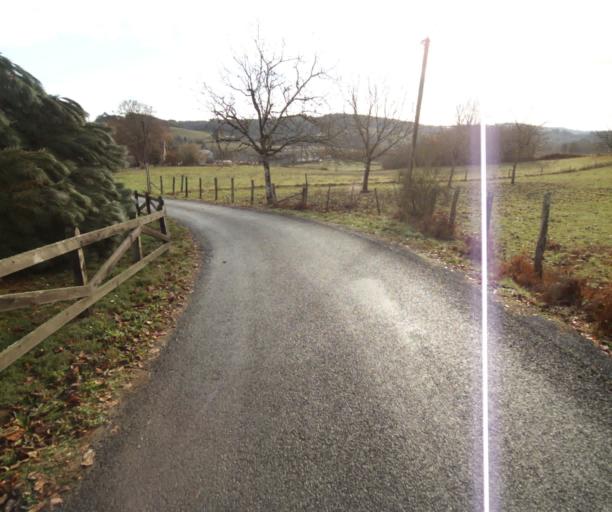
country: FR
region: Limousin
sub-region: Departement de la Correze
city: Saint-Mexant
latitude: 45.2489
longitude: 1.6361
